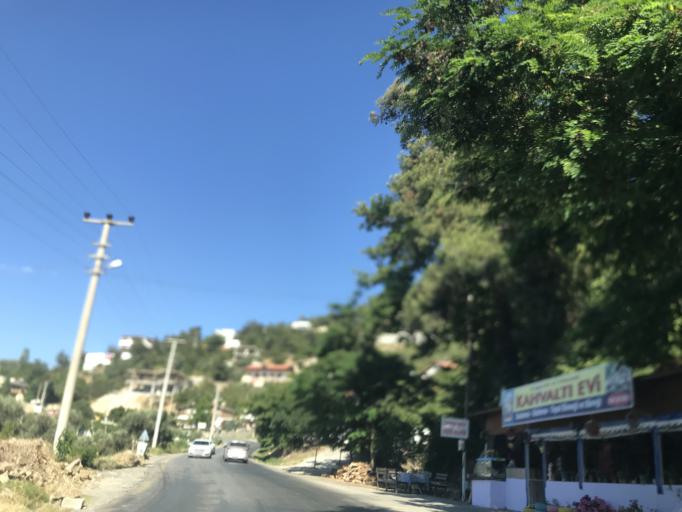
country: TR
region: Aydin
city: Davutlar
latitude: 37.7364
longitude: 27.3382
